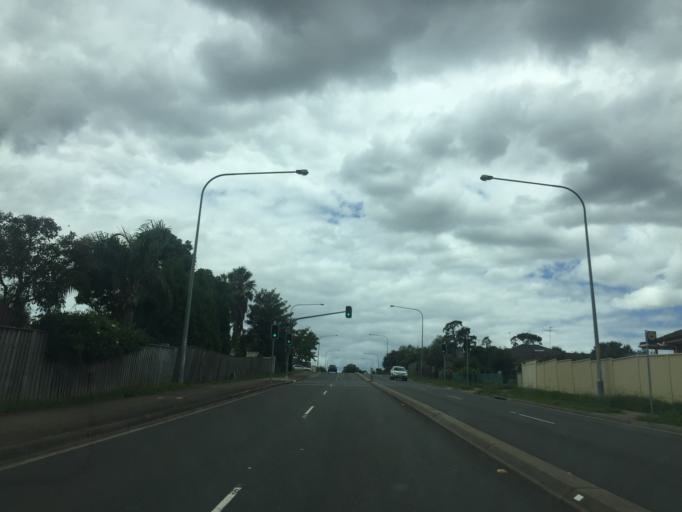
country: AU
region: New South Wales
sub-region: Blacktown
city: Quakers Hill
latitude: -33.7124
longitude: 150.8889
